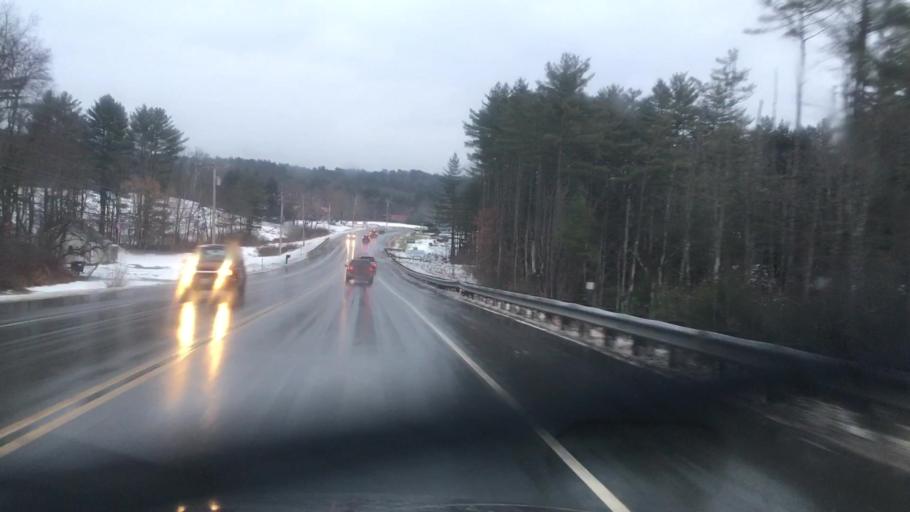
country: US
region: New Hampshire
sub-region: Sullivan County
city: Newport
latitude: 43.3646
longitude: -72.2324
